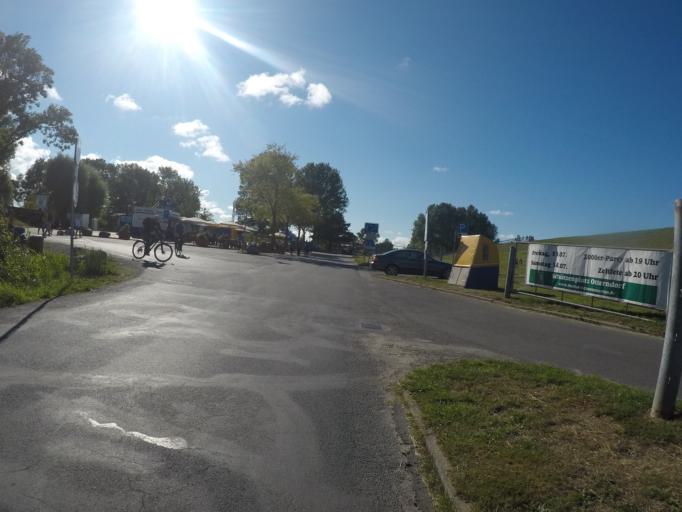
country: DE
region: Lower Saxony
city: Otterndorf
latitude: 53.8259
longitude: 8.8844
